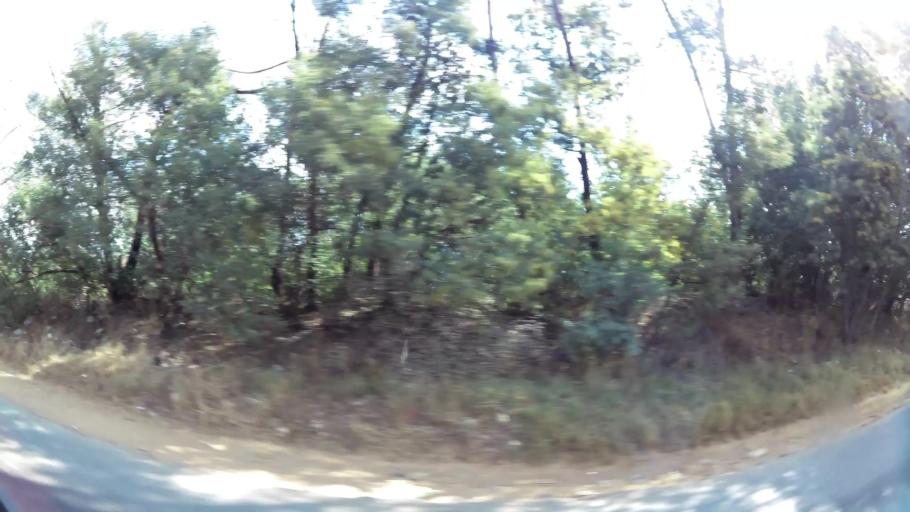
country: ZA
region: Gauteng
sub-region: City of Johannesburg Metropolitan Municipality
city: Roodepoort
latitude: -26.1766
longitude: 27.8718
